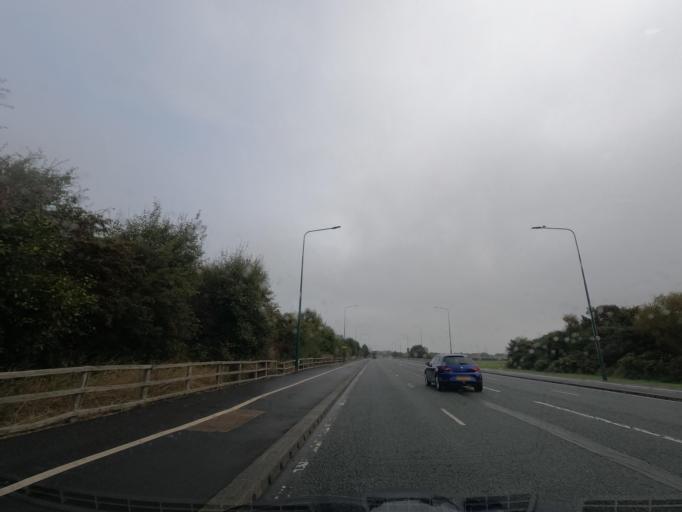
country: GB
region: England
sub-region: Redcar and Cleveland
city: Redcar
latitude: 54.6107
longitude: -1.0967
